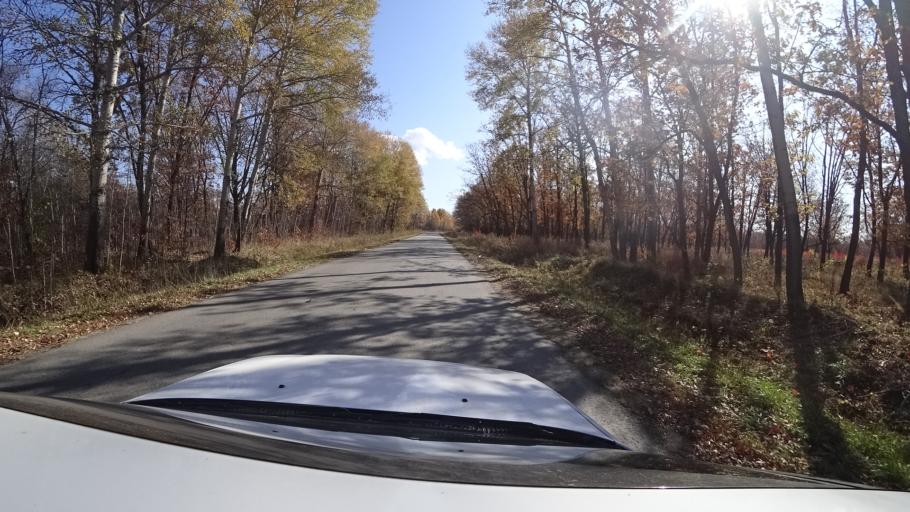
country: RU
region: Primorskiy
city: Lazo
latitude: 45.8712
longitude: 133.6579
